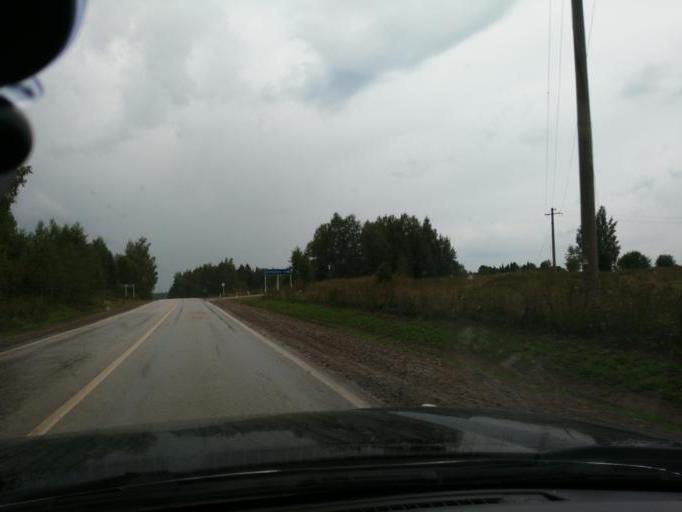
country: RU
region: Perm
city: Barda
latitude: 56.8848
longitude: 55.8320
